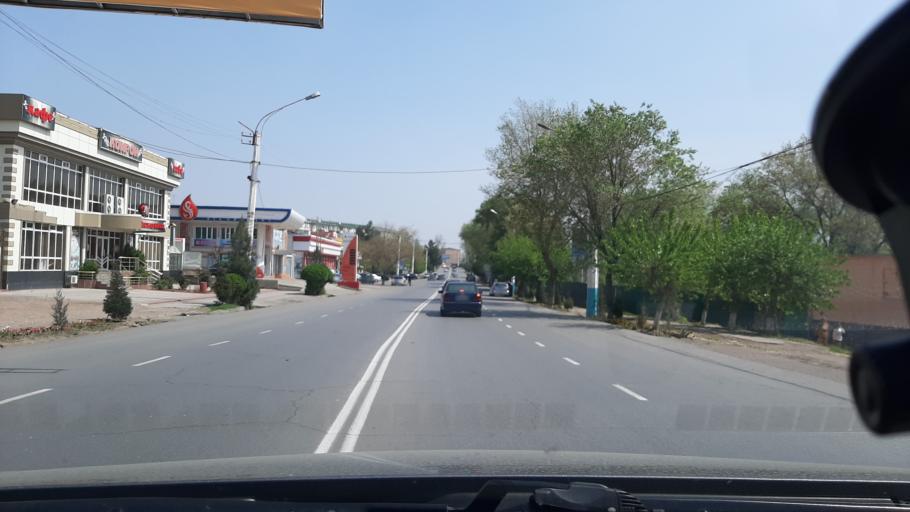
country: TJ
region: Viloyati Sughd
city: Khujand
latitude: 40.2949
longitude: 69.6014
